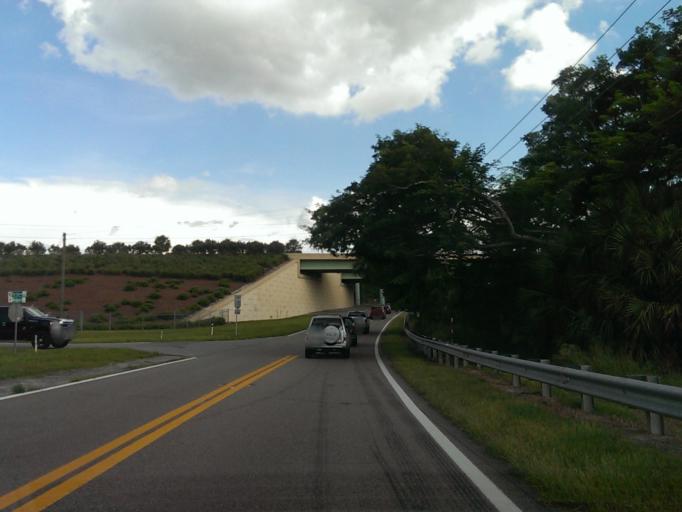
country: US
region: Florida
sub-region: Orange County
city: Oakland
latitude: 28.4600
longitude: -81.6374
